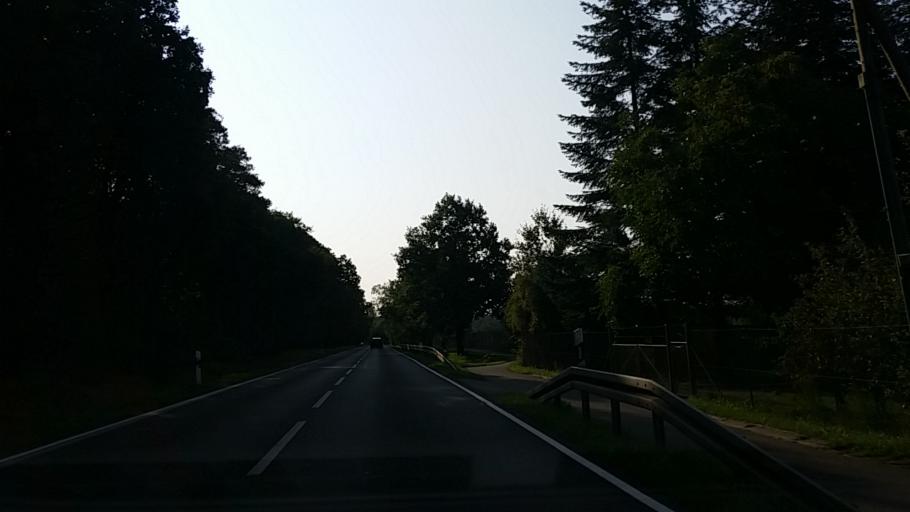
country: DE
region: Mecklenburg-Vorpommern
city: Wittenburg
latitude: 53.4918
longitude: 11.1001
